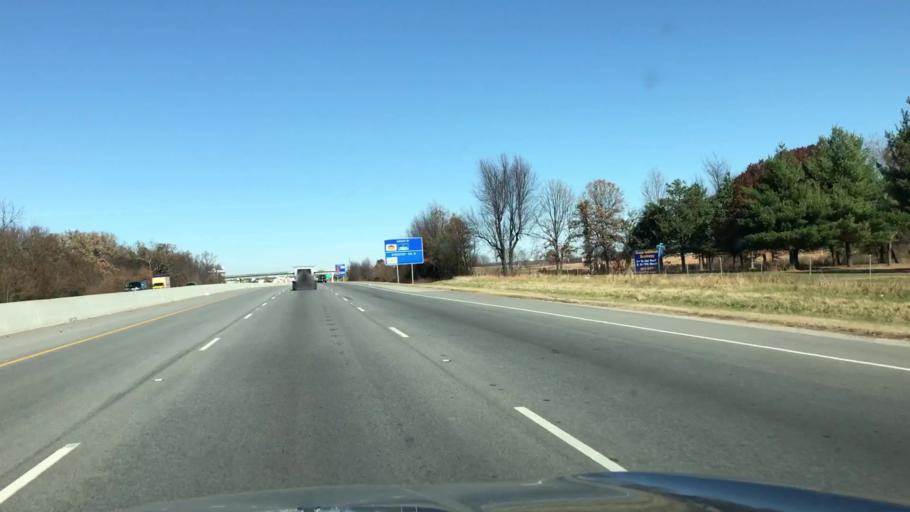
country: US
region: Arkansas
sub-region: Benton County
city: Lowell
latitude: 36.2609
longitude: -94.1502
